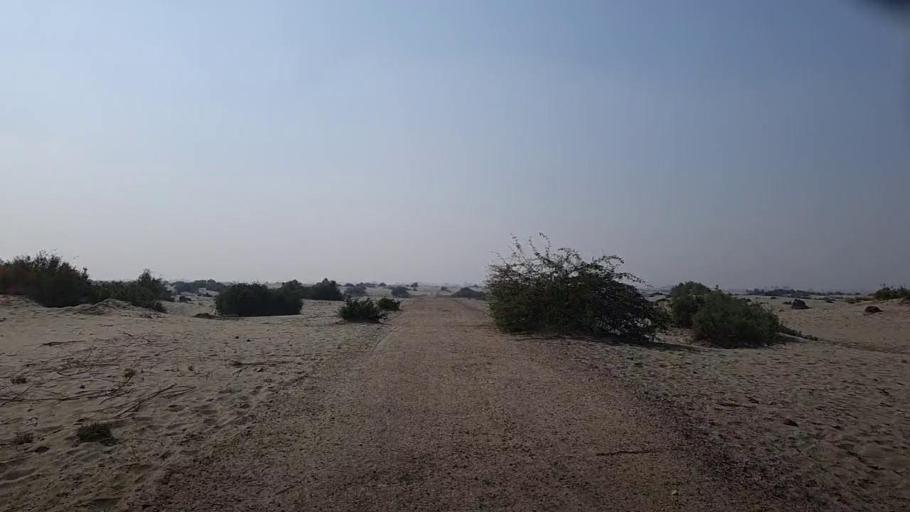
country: PK
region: Sindh
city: Bozdar
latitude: 27.2261
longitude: 68.5885
